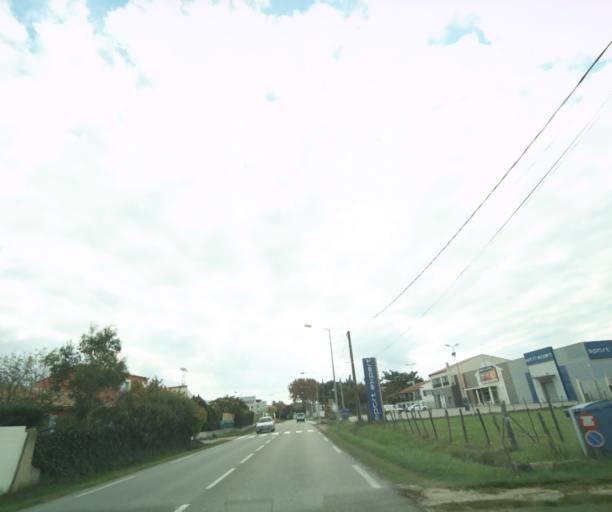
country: FR
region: Languedoc-Roussillon
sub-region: Departement du Gard
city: Aigues-Mortes
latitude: 43.5746
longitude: 4.1963
